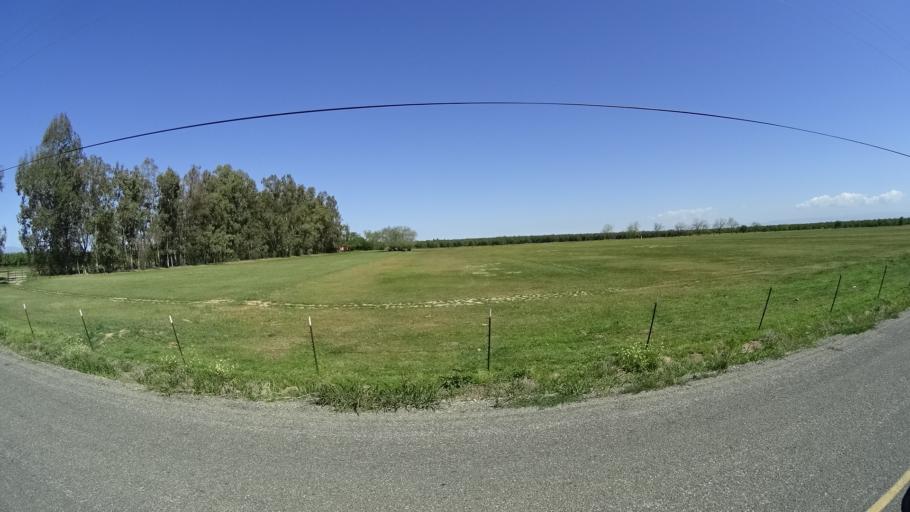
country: US
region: California
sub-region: Glenn County
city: Orland
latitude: 39.6964
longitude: -122.1722
